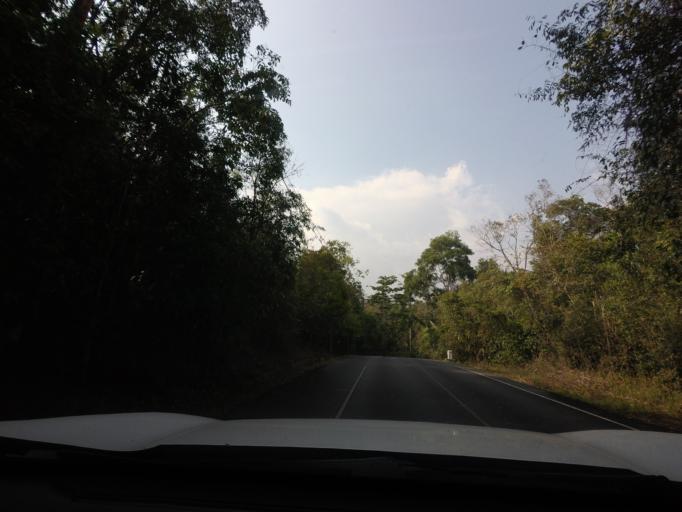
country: TH
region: Nakhon Ratchasima
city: Pak Chong
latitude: 14.4261
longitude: 101.3932
